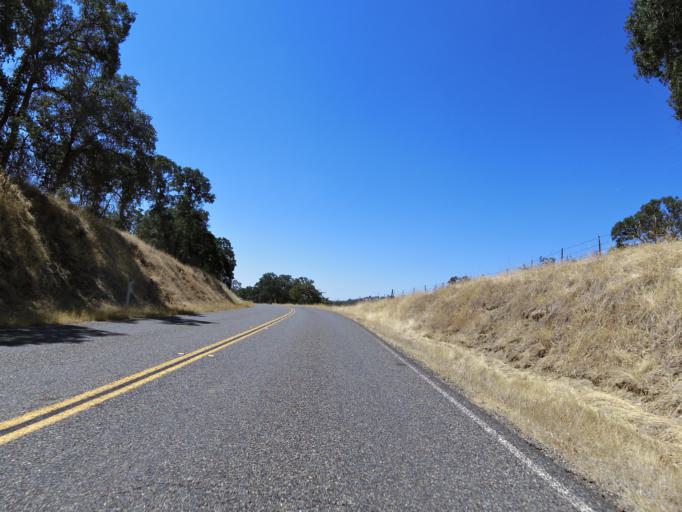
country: US
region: California
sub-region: Mariposa County
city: Mariposa
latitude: 37.4589
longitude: -120.1048
